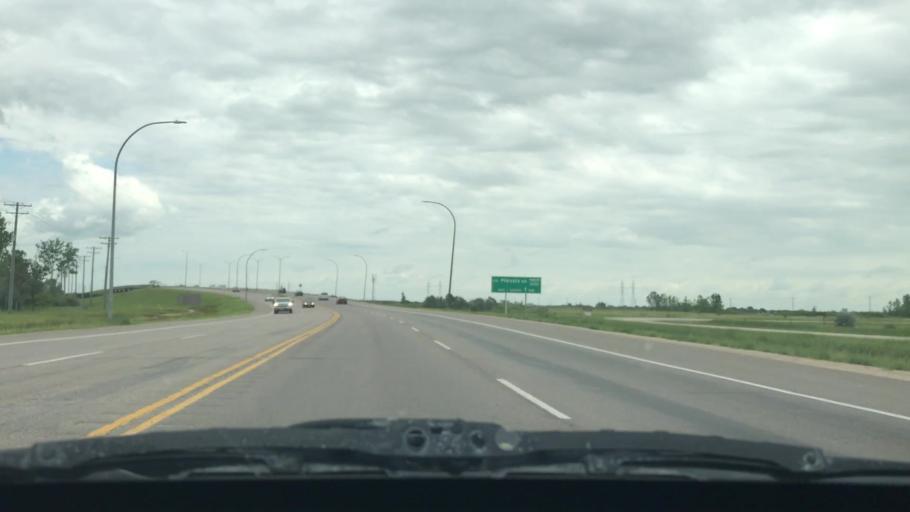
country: CA
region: Manitoba
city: Winnipeg
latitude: 49.8554
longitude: -97.0291
